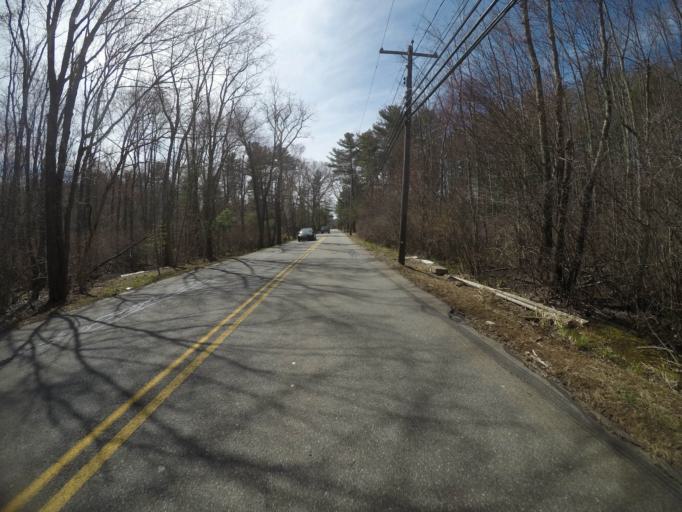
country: US
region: Massachusetts
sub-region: Bristol County
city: Easton
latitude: 42.0244
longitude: -71.0715
